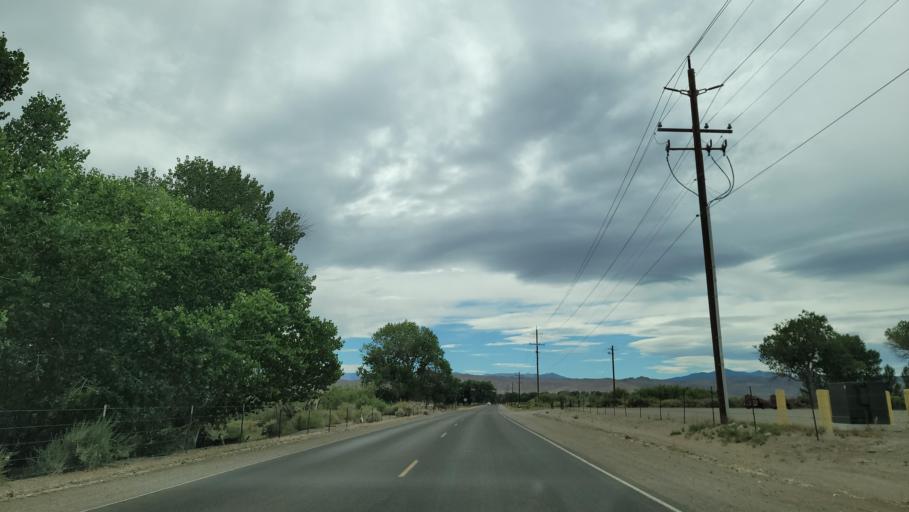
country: US
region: Nevada
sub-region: Lyon County
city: Yerington
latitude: 39.0481
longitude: -119.1628
